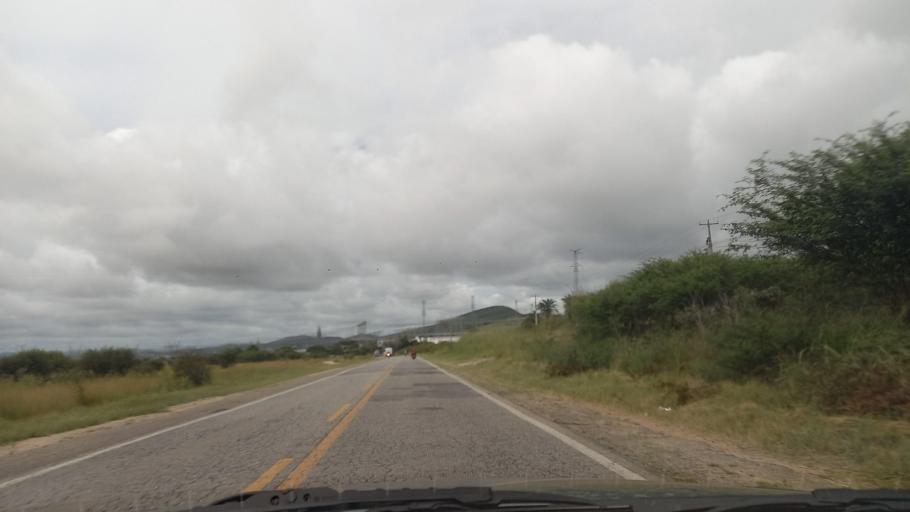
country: BR
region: Pernambuco
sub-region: Sao Joao
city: Sao Joao
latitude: -8.8808
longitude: -36.4108
